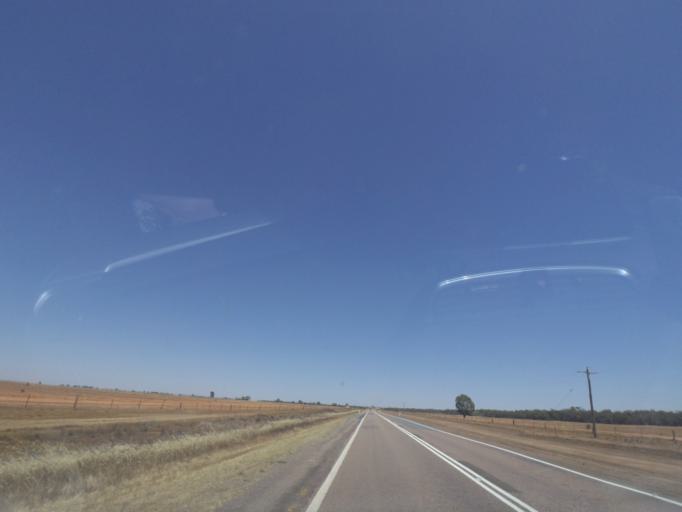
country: AU
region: New South Wales
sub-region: Berrigan
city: Berrigan
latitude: -35.1495
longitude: 145.9978
